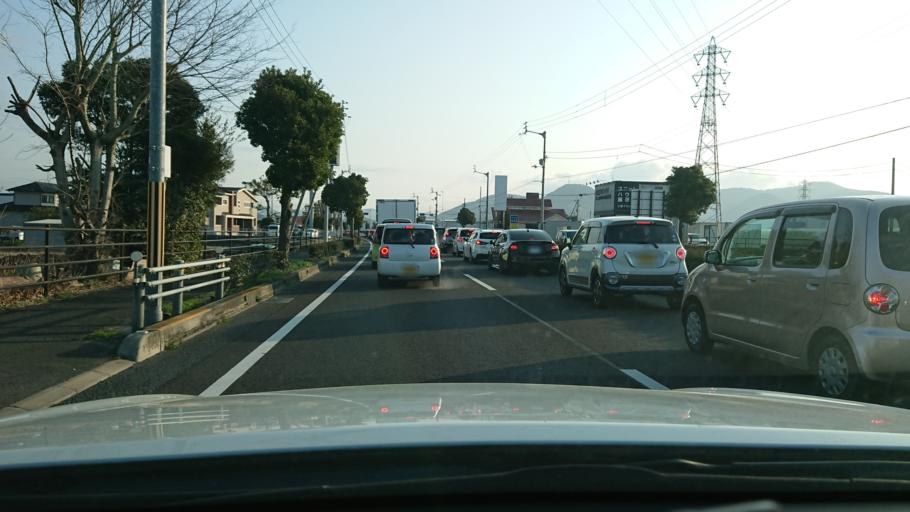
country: JP
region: Kagawa
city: Sakaidecho
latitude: 34.2848
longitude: 133.8262
